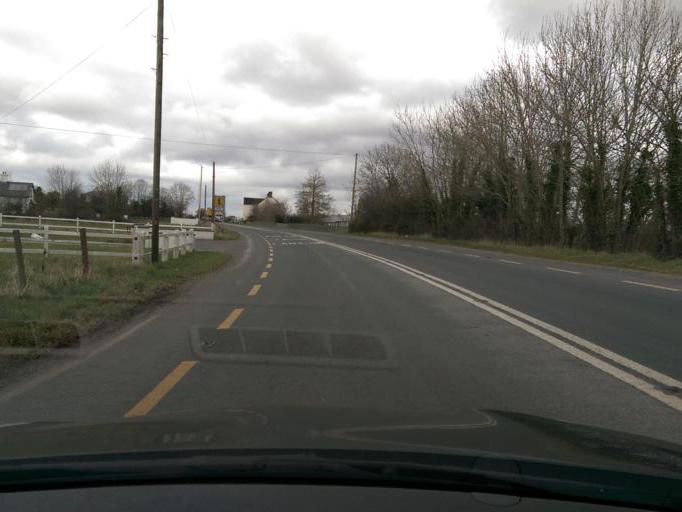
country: IE
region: Leinster
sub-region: An Iarmhi
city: Athlone
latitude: 53.3746
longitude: -8.0080
